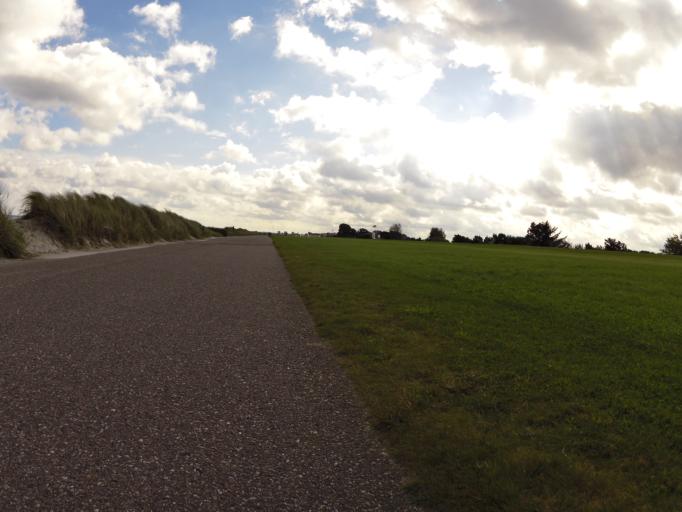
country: DE
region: Schleswig-Holstein
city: Krummbek
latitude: 54.4208
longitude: 10.4018
